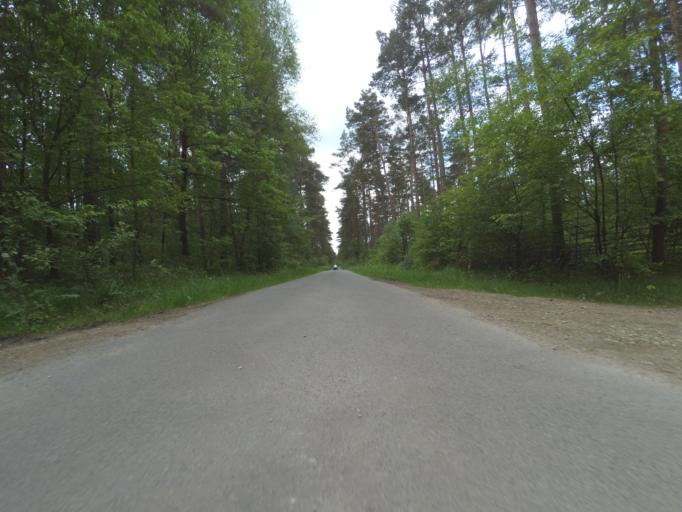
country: DE
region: Lower Saxony
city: Wietze
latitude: 52.6296
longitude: 9.8024
